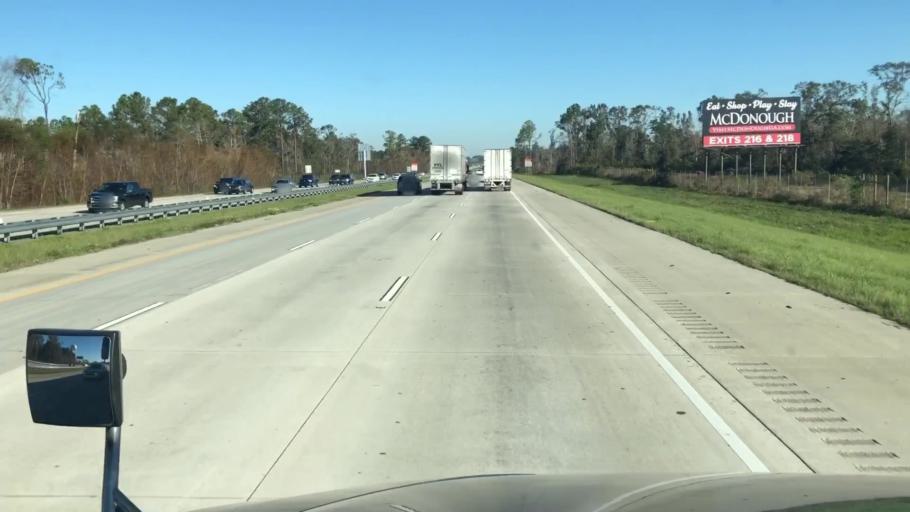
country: US
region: Georgia
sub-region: Dooly County
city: Vienna
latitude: 32.0967
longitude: -83.7629
